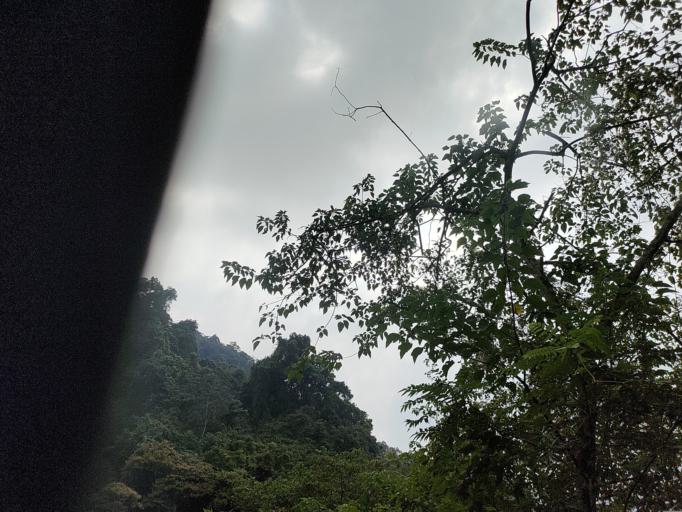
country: TW
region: Taiwan
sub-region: Hsinchu
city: Hsinchu
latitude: 24.6271
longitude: 121.0658
